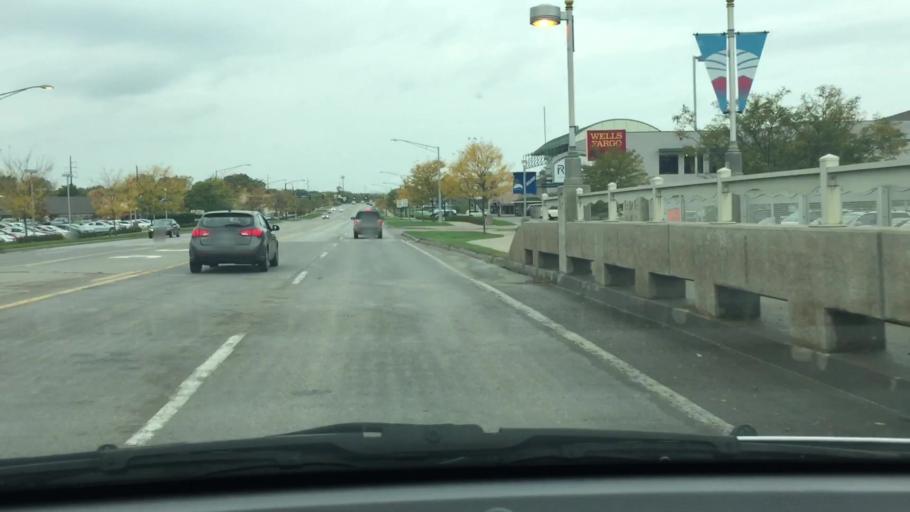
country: US
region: Iowa
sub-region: Johnson County
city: Coralville
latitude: 41.6708
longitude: -91.5713
